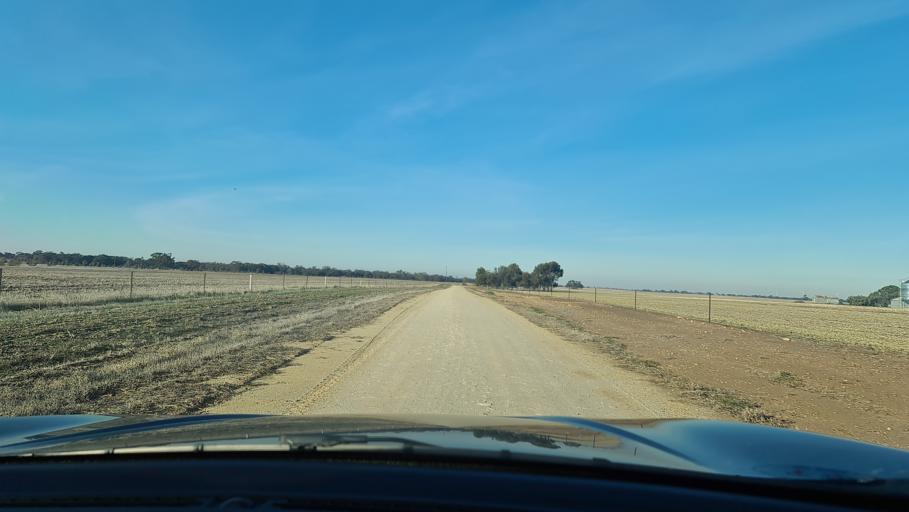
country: AU
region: Victoria
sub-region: Horsham
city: Horsham
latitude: -36.3621
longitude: 142.3958
